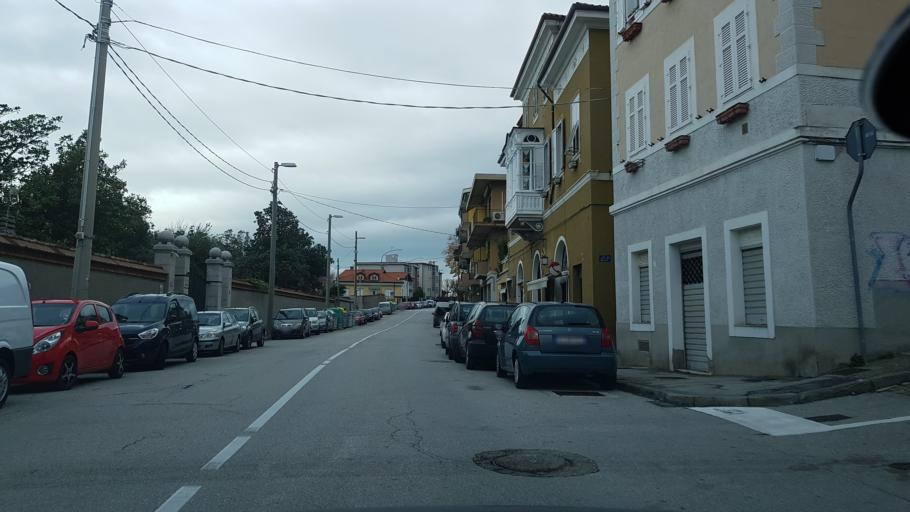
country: IT
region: Friuli Venezia Giulia
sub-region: Provincia di Trieste
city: Villa Opicina
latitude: 45.6703
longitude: 13.7618
